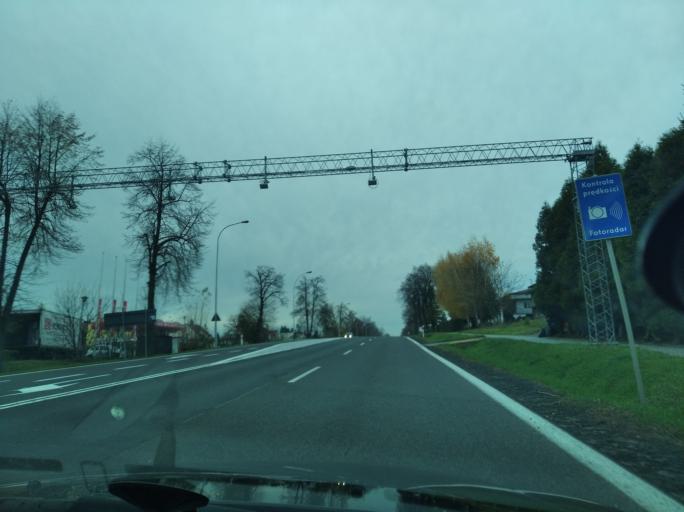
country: PL
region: Subcarpathian Voivodeship
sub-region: Powiat przeworski
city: Przeworsk
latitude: 50.0608
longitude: 22.4782
